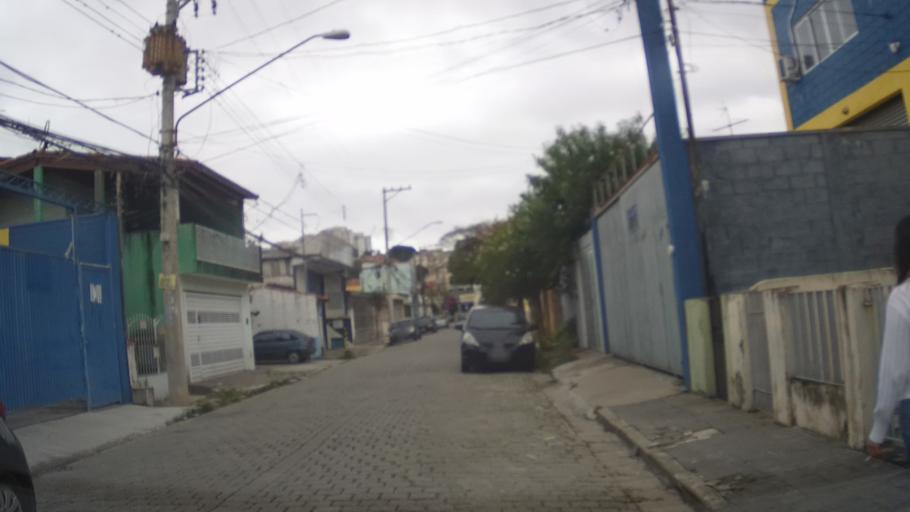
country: BR
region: Sao Paulo
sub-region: Guarulhos
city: Guarulhos
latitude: -23.5018
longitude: -46.5492
